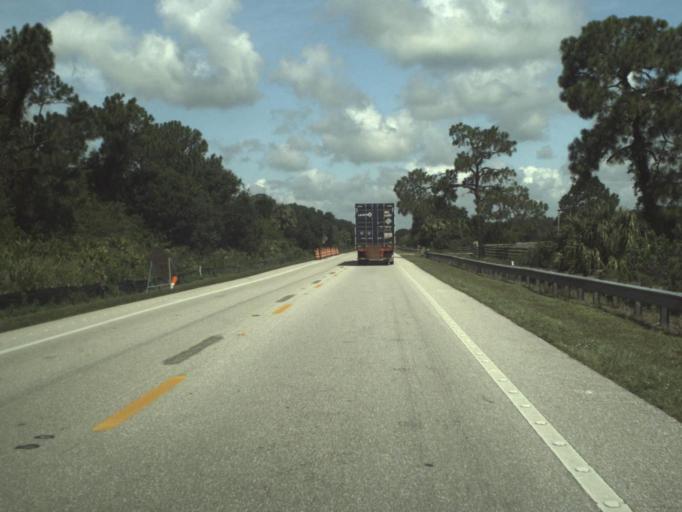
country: US
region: Florida
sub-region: Martin County
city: Indiantown
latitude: 27.0684
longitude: -80.5404
